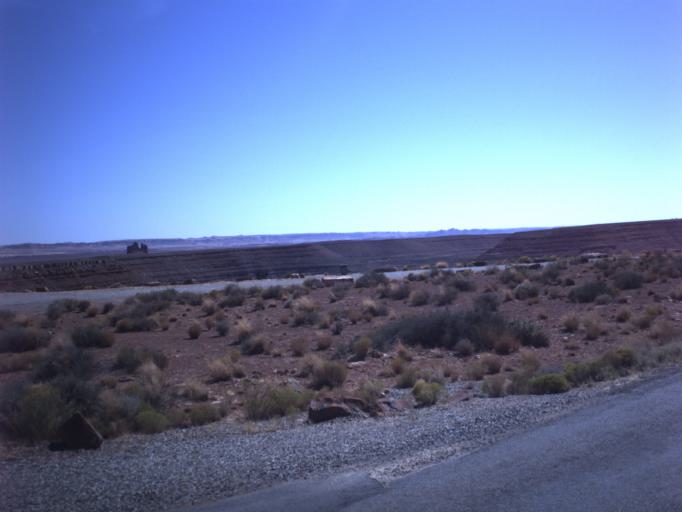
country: US
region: Arizona
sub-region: Navajo County
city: Kayenta
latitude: 37.1751
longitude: -109.9267
